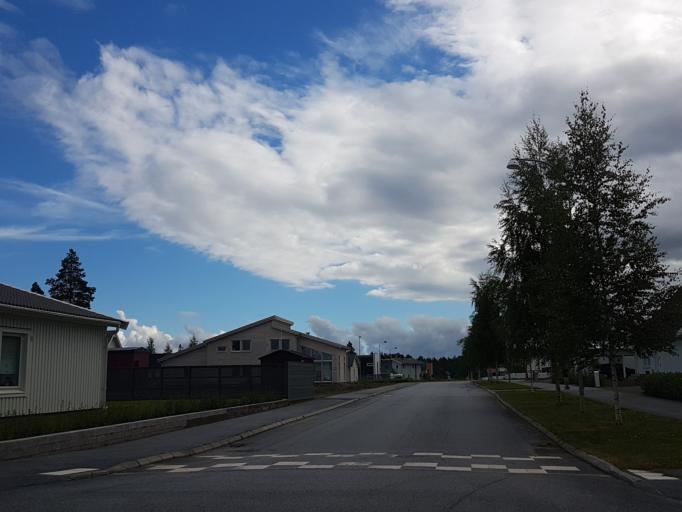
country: SE
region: Vaesterbotten
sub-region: Umea Kommun
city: Ersmark
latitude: 63.8042
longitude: 20.3694
